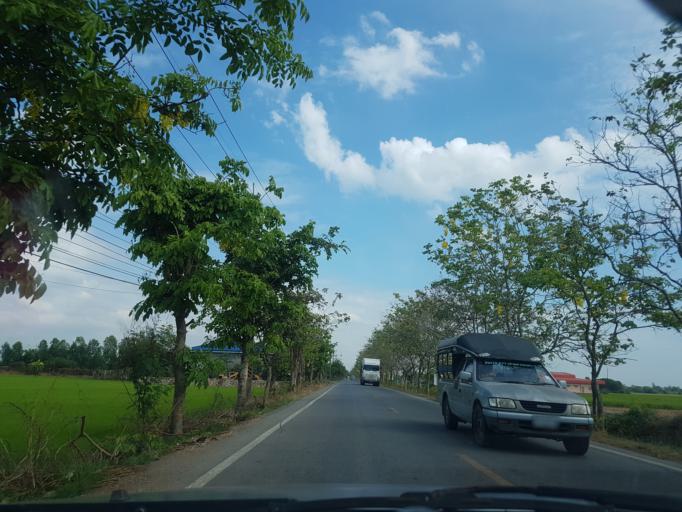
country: TH
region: Pathum Thani
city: Nong Suea
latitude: 14.1357
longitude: 100.8812
